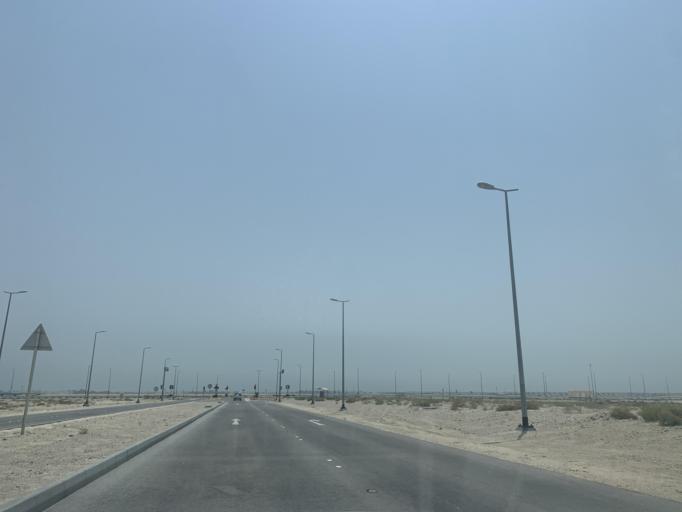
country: BH
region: Central Governorate
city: Dar Kulayb
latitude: 25.8386
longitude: 50.5905
